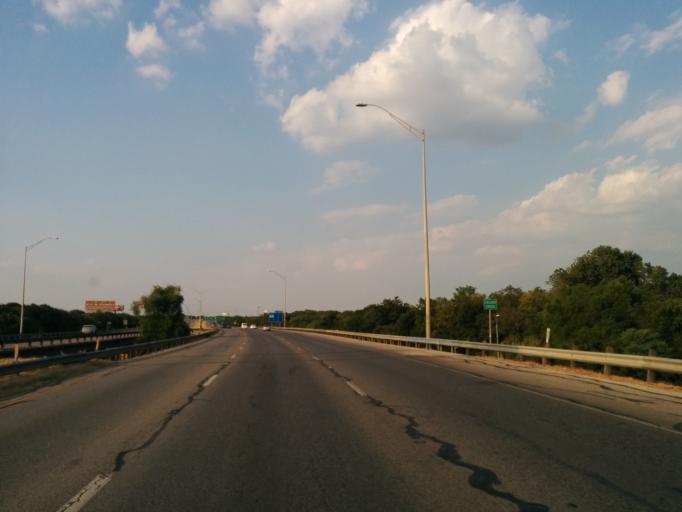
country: US
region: Texas
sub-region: Bexar County
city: Kirby
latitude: 29.4172
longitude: -98.4271
